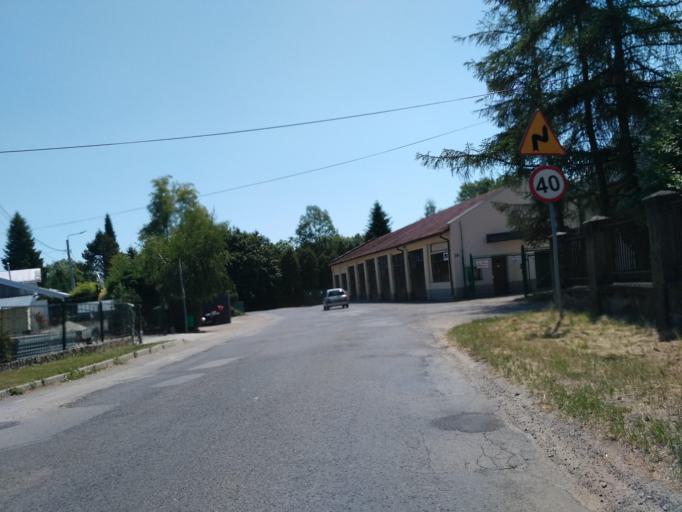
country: PL
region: Subcarpathian Voivodeship
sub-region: Krosno
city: Krosno
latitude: 49.6963
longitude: 21.7852
